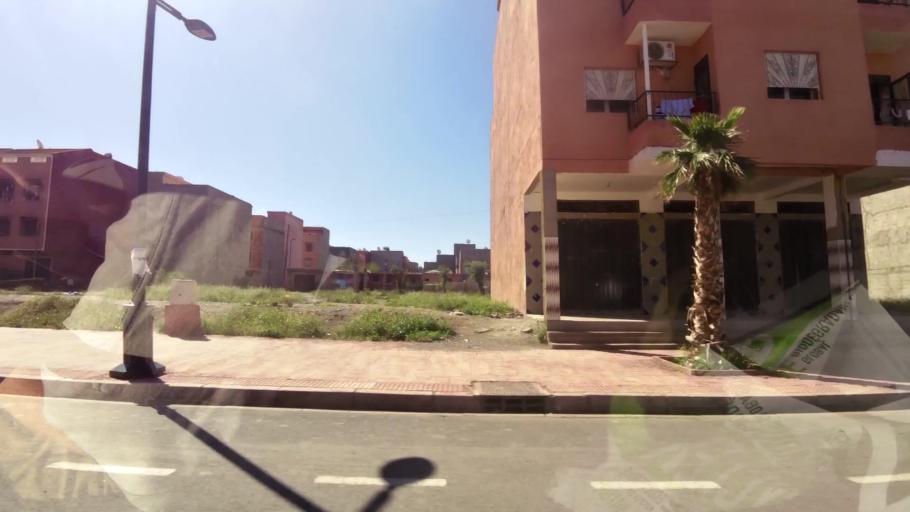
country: MA
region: Marrakech-Tensift-Al Haouz
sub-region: Marrakech
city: Marrakesh
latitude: 31.5934
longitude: -8.0435
